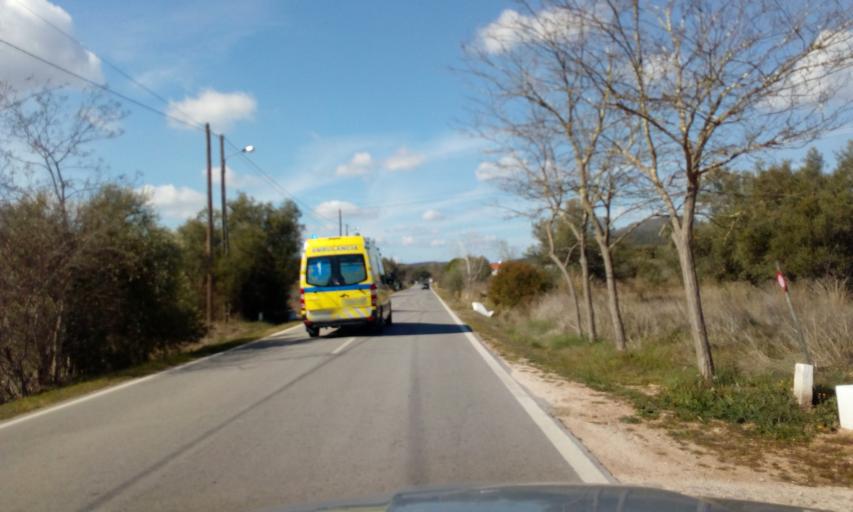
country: PT
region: Faro
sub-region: Loule
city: Loule
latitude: 37.2442
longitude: -8.0538
